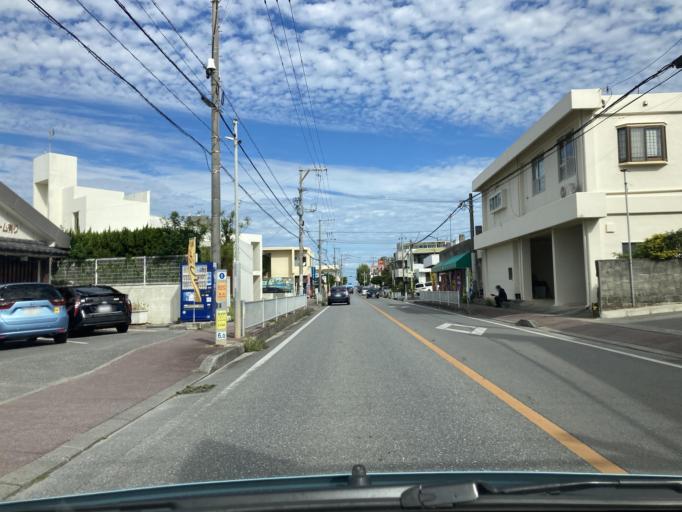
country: JP
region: Okinawa
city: Ishikawa
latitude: 26.4124
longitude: 127.7323
